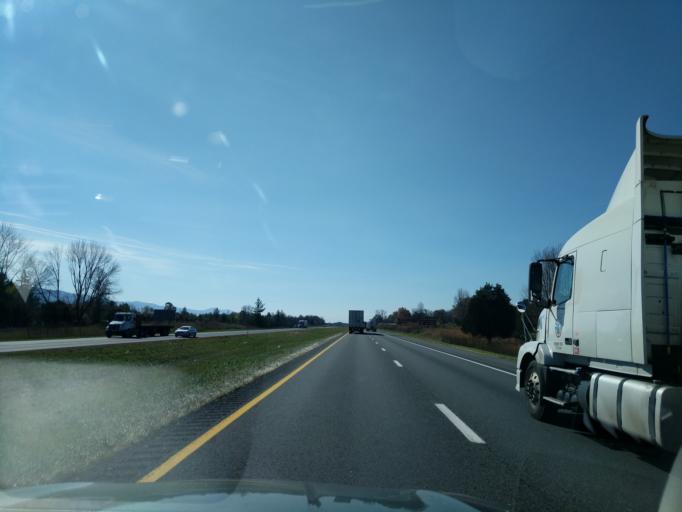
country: US
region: Virginia
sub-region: Shenandoah County
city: New Market
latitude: 38.6603
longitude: -78.6684
